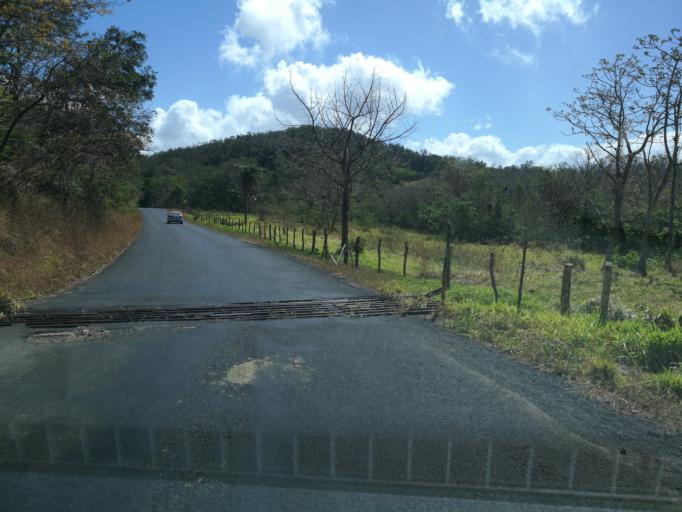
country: CR
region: Guanacaste
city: Liberia
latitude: 10.7460
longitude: -85.3791
